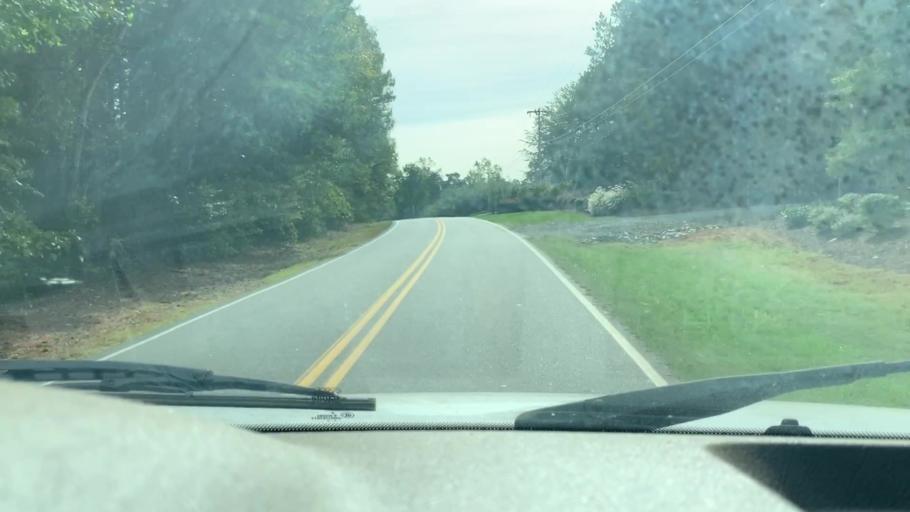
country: US
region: North Carolina
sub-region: Catawba County
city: Lake Norman of Catawba
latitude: 35.5688
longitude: -80.9333
